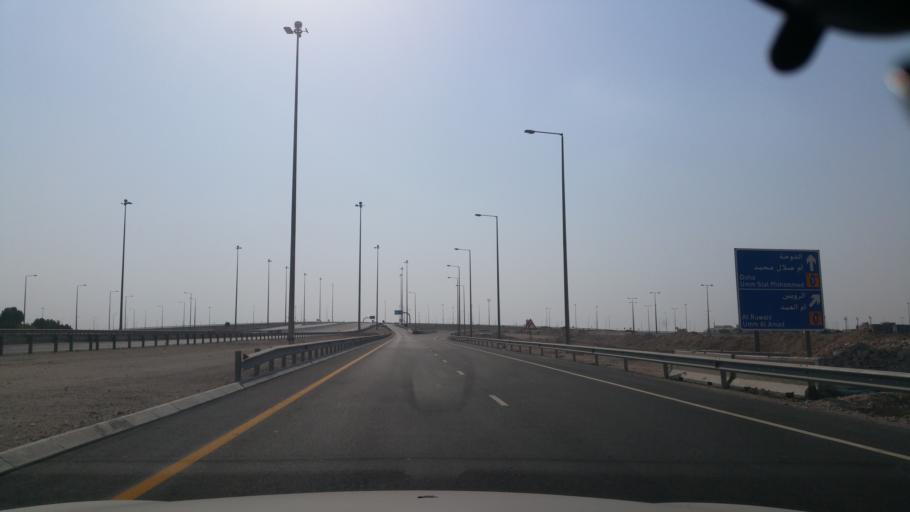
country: QA
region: Baladiyat Umm Salal
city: Umm Salal `Ali
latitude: 25.4502
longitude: 51.4162
